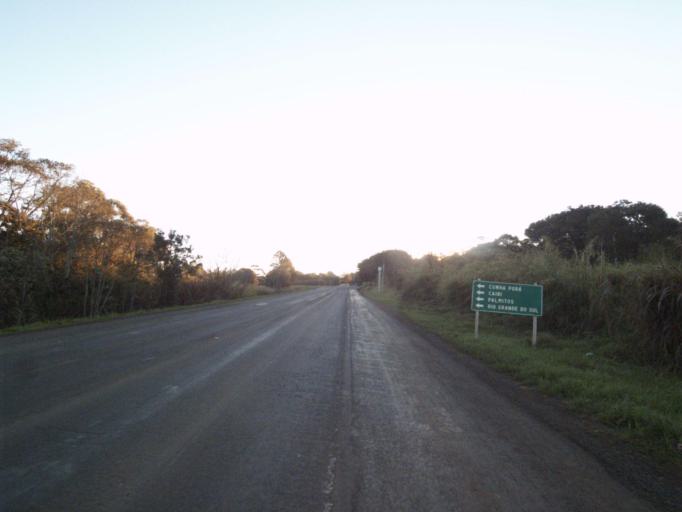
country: BR
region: Santa Catarina
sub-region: Sao Lourenco Do Oeste
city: Sao Lourenco dOeste
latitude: -26.8059
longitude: -53.1790
